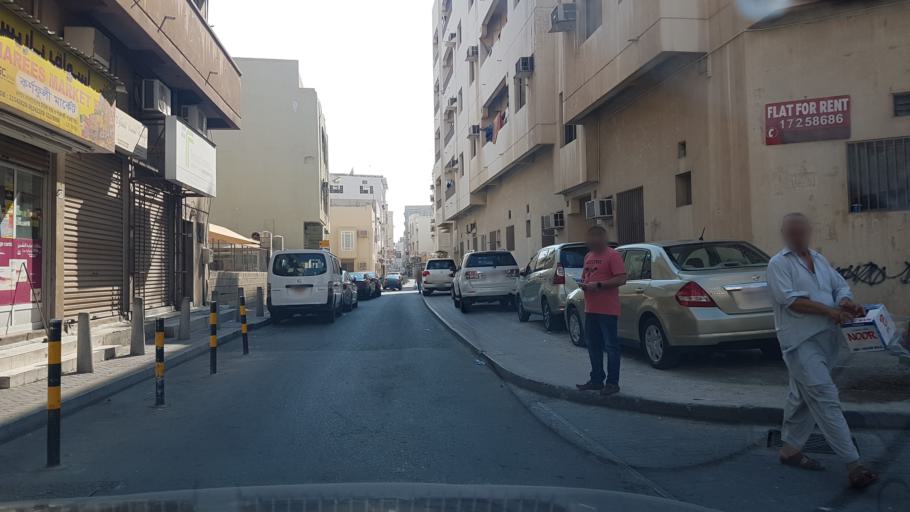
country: BH
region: Manama
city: Manama
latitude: 26.2341
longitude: 50.5800
